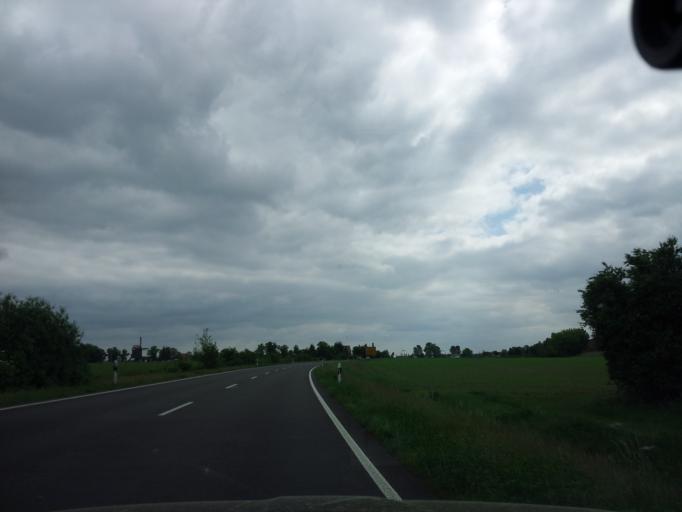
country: DE
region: Brandenburg
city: Beelitz
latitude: 52.2382
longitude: 12.9878
